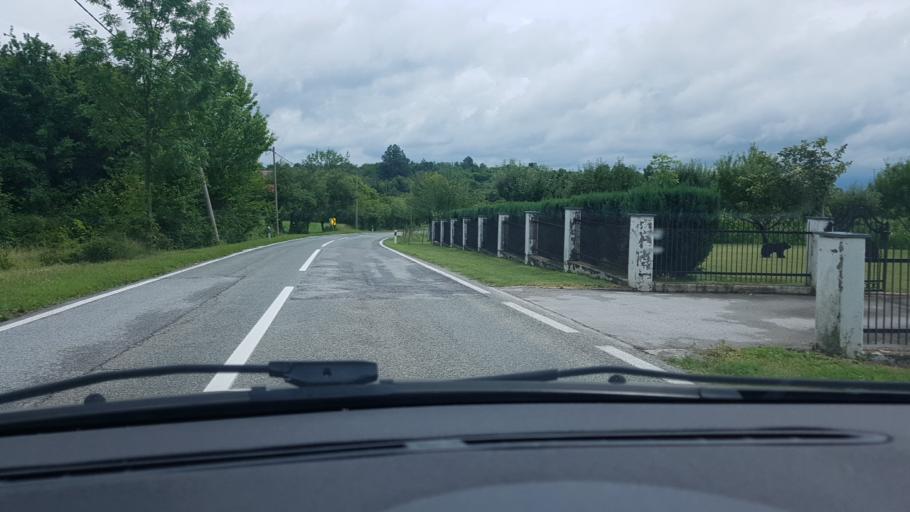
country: HR
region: Licko-Senjska
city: Jezerce
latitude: 44.9471
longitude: 15.6760
